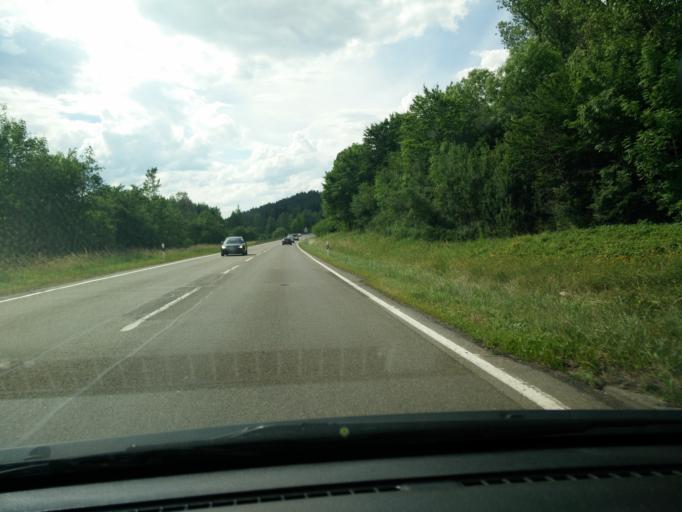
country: DE
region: Baden-Wuerttemberg
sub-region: Freiburg Region
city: Trossingen
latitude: 48.0801
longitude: 8.6148
